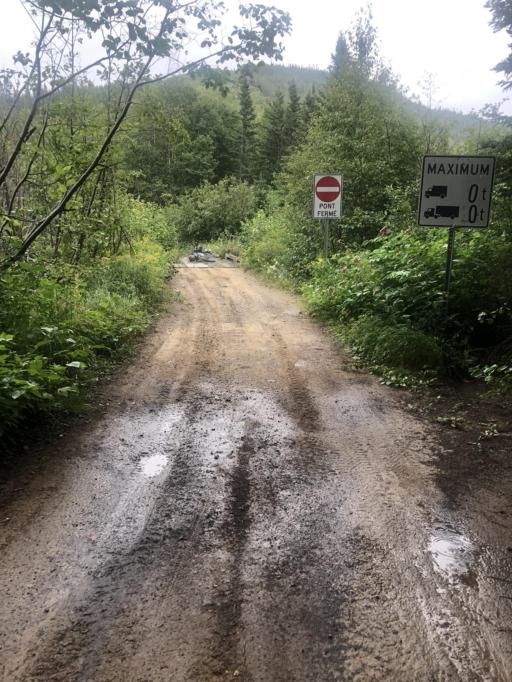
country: CA
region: Quebec
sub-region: Capitale-Nationale
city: La Malbaie
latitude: 47.8321
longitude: -70.4623
